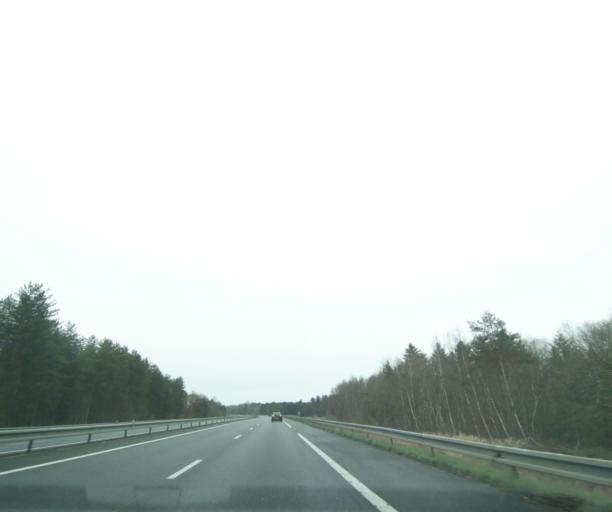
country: FR
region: Centre
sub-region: Departement du Loir-et-Cher
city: Nouan-le-Fuzelier
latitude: 47.5345
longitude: 2.0046
